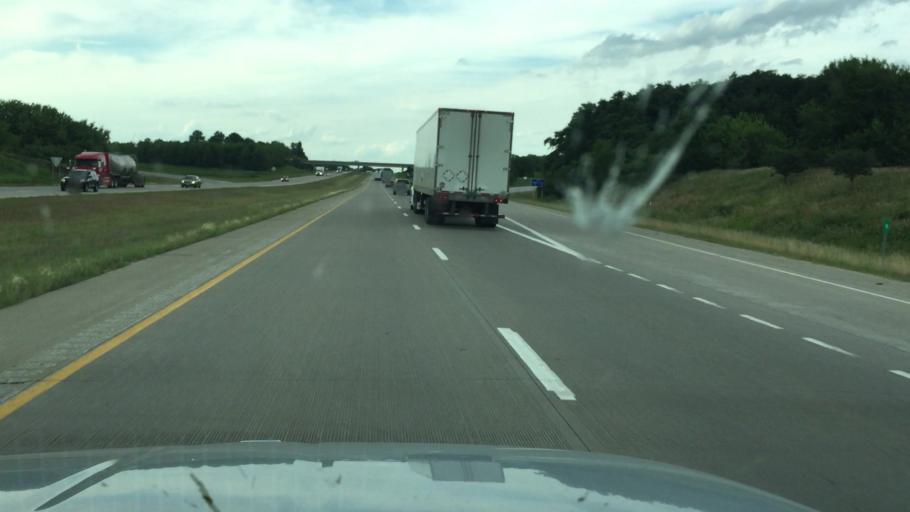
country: US
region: Iowa
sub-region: Scott County
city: Buffalo
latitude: 41.5331
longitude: -90.6753
